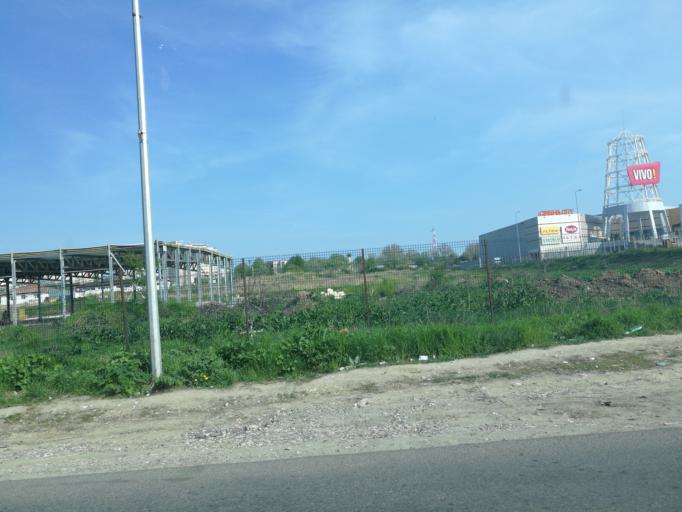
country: RO
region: Constanta
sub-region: Municipiul Constanta
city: Palazu Mare
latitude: 44.2018
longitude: 28.6090
